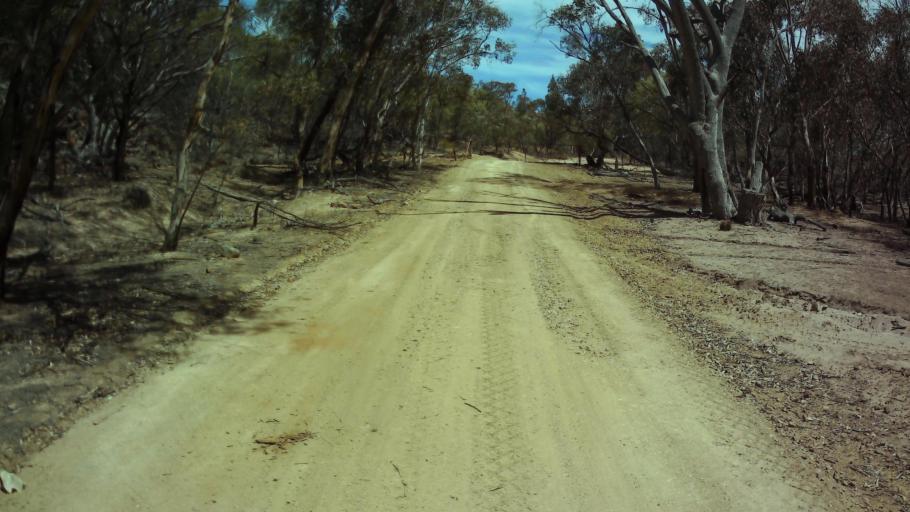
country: AU
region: New South Wales
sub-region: Weddin
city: Grenfell
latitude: -33.8044
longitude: 148.1605
